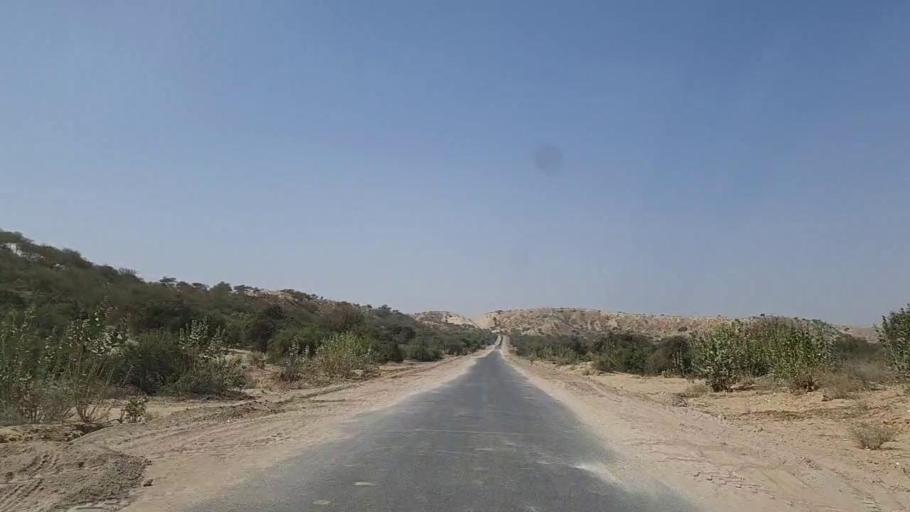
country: PK
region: Sindh
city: Diplo
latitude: 24.5862
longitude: 69.5289
